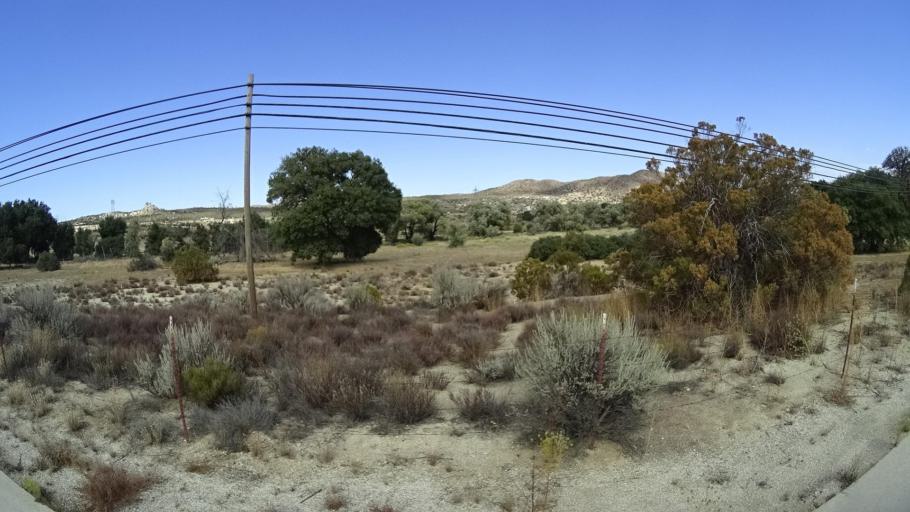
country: MX
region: Baja California
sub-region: Tecate
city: Cereso del Hongo
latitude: 32.6600
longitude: -116.2556
